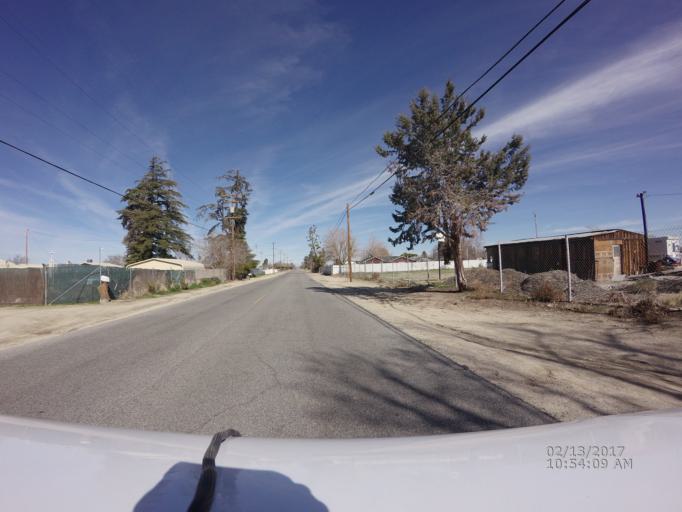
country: US
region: California
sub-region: Los Angeles County
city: Littlerock
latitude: 34.5342
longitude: -117.9837
